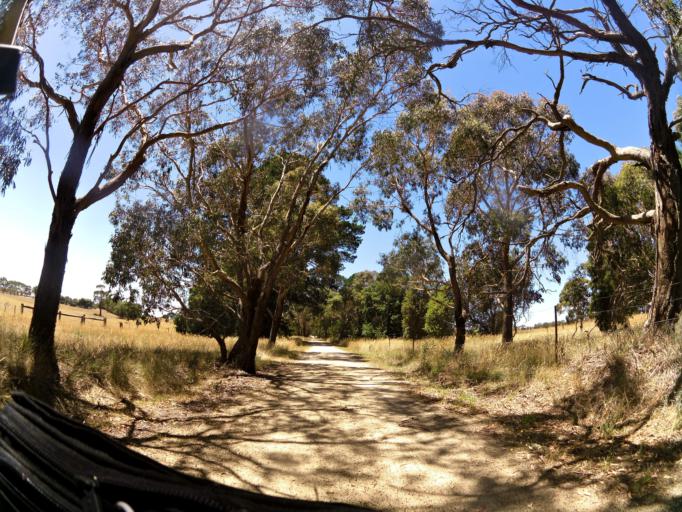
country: AU
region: Victoria
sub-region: Ballarat North
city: Delacombe
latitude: -37.5591
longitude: 143.7423
